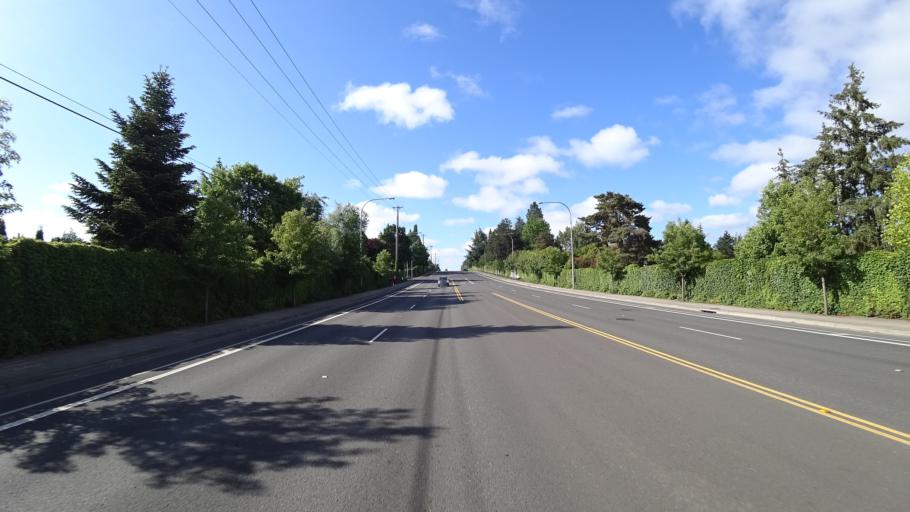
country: US
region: Oregon
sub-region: Washington County
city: Bethany
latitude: 45.5557
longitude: -122.8676
